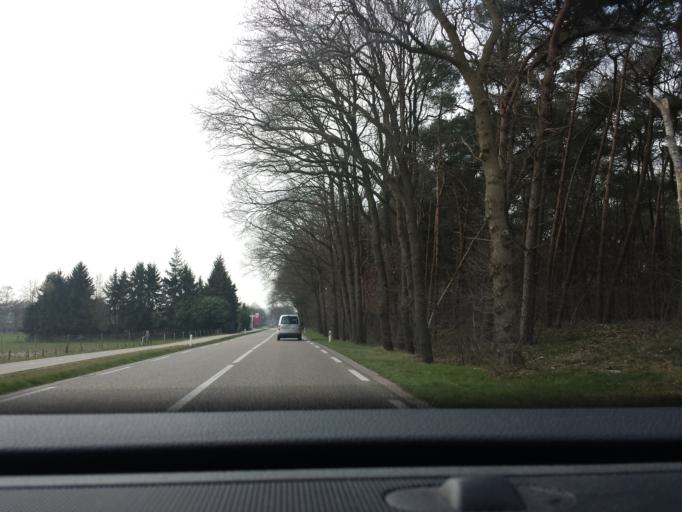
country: NL
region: Gelderland
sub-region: Gemeente Bronckhorst
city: Zelhem
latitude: 52.0019
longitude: 6.3972
